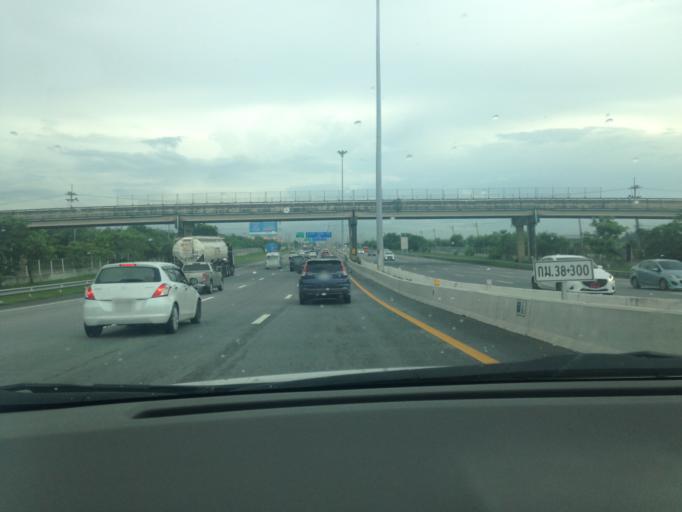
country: TH
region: Chachoengsao
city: Bang Pakong
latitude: 13.6099
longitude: 100.9380
